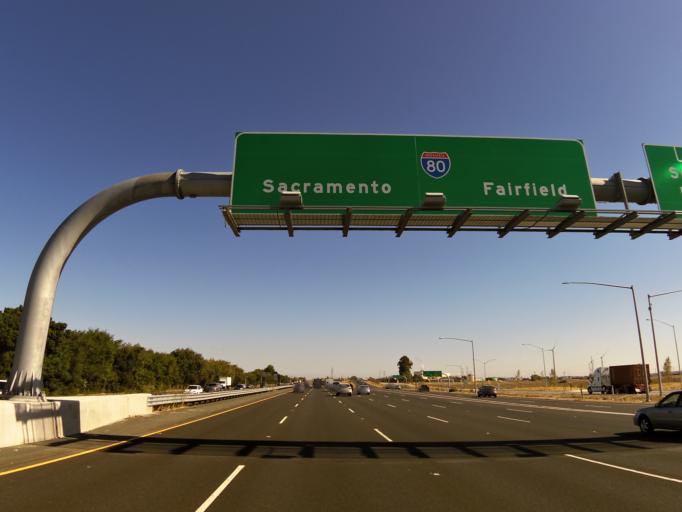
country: US
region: California
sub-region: Solano County
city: Green Valley
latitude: 38.2331
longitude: -122.1081
